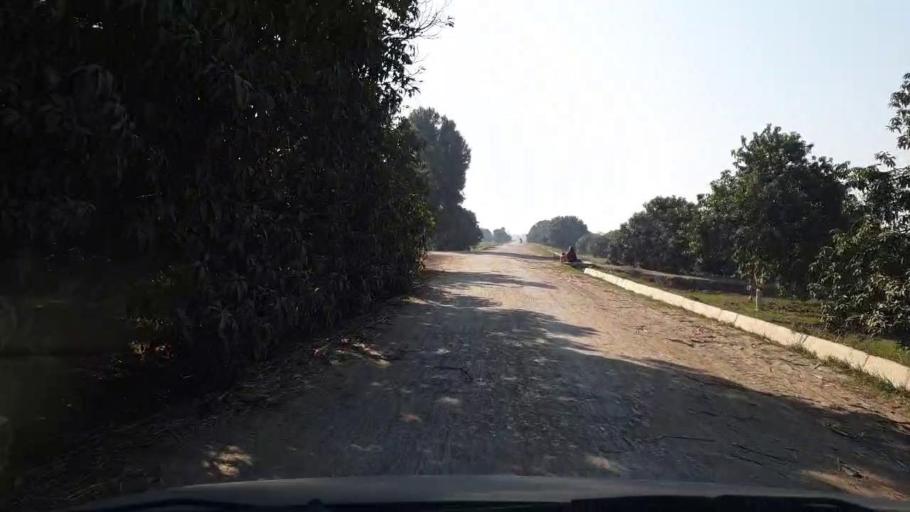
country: PK
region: Sindh
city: Tando Jam
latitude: 25.4360
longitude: 68.6033
